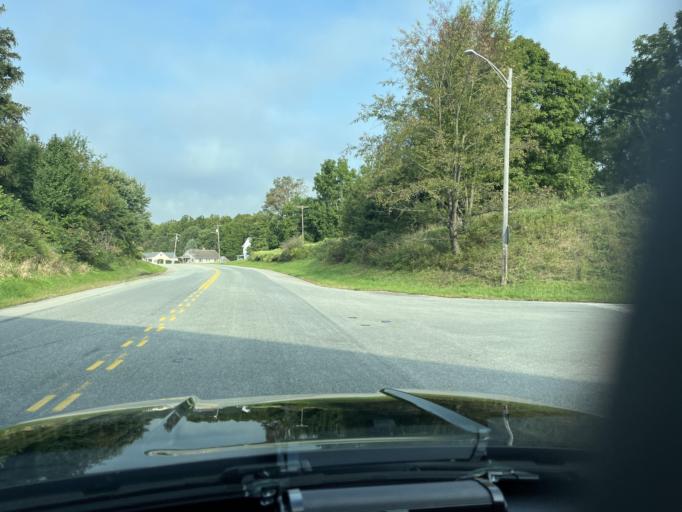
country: US
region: Pennsylvania
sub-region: Fayette County
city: Hopwood
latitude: 39.8727
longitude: -79.7091
